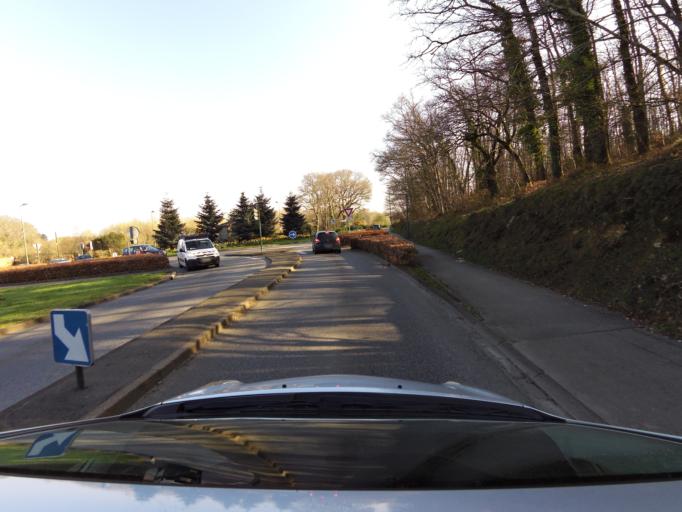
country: FR
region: Brittany
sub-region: Departement du Morbihan
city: Gestel
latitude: 47.7958
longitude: -3.4827
